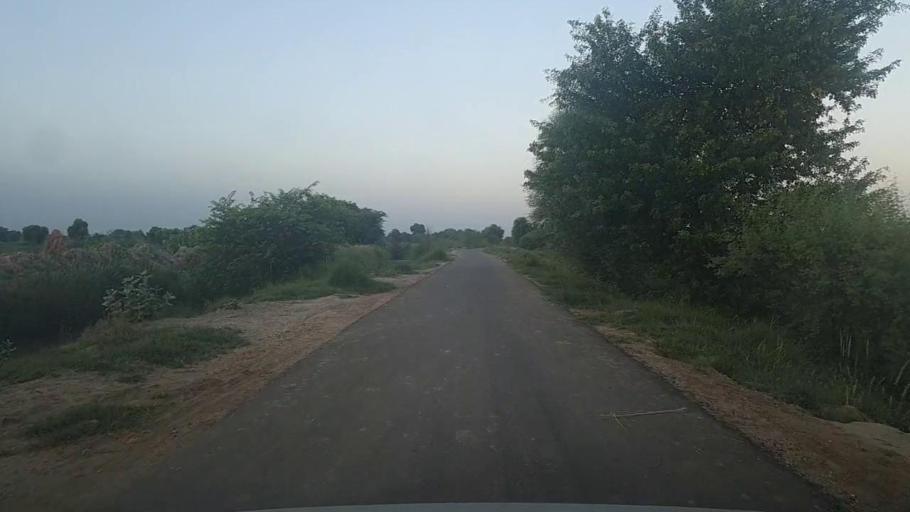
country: PK
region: Sindh
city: Khairpur
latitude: 28.0933
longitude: 69.7332
